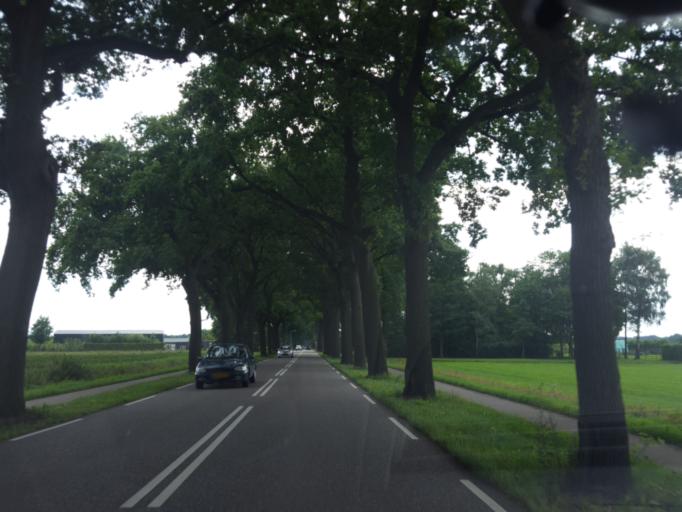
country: NL
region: Limburg
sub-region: Gemeente Bergen
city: Wellerlooi
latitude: 51.4791
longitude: 6.0714
